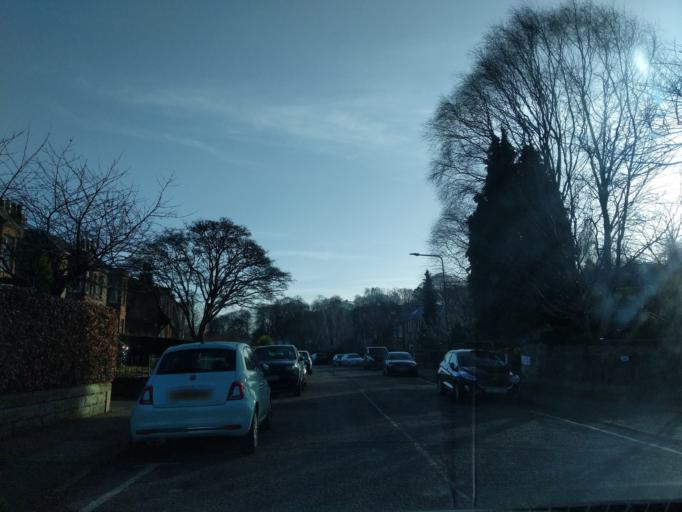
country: GB
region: Scotland
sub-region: Edinburgh
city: Colinton
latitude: 55.9561
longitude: -3.2537
